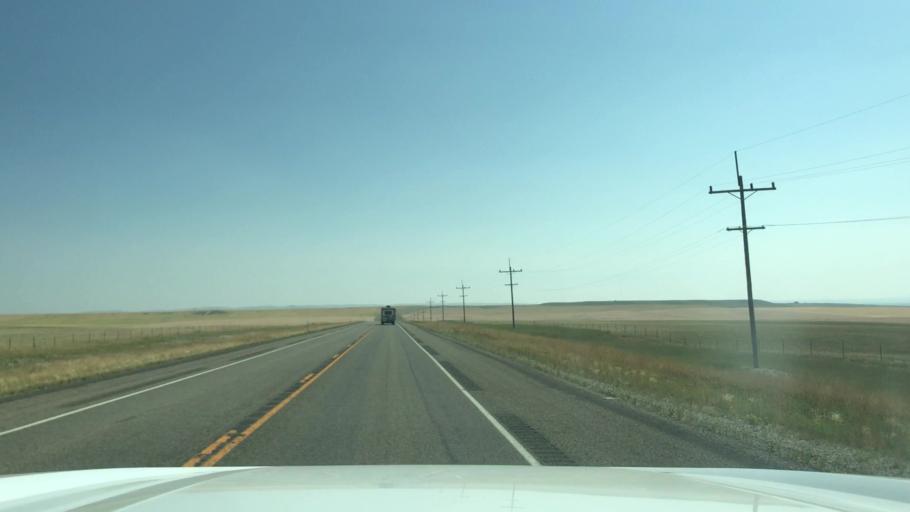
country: US
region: Montana
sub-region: Wheatland County
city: Harlowton
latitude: 46.4965
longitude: -109.7661
